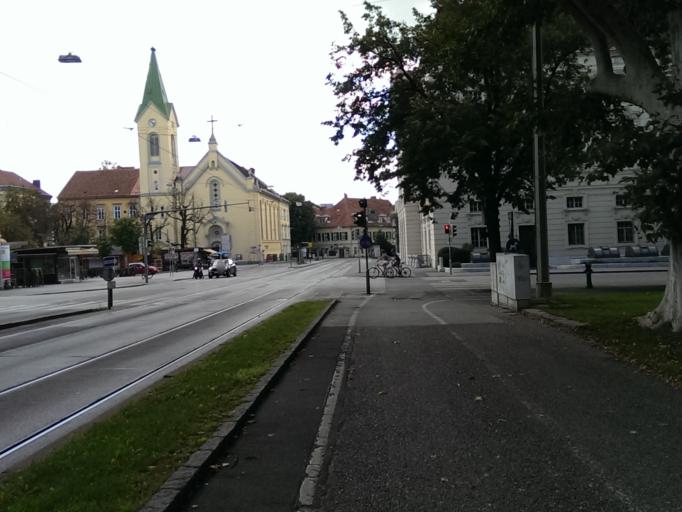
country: AT
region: Styria
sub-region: Graz Stadt
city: Graz
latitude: 47.0693
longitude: 15.4466
